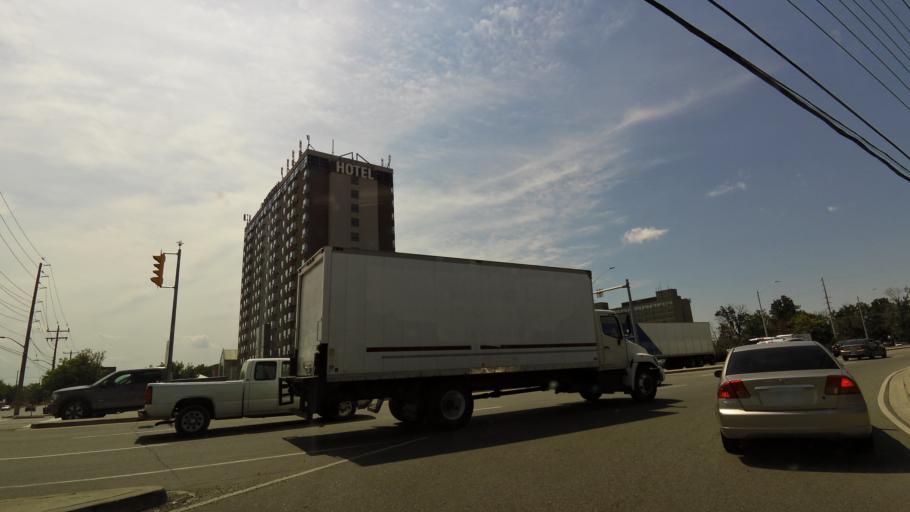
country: CA
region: Ontario
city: Etobicoke
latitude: 43.6429
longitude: -79.6302
